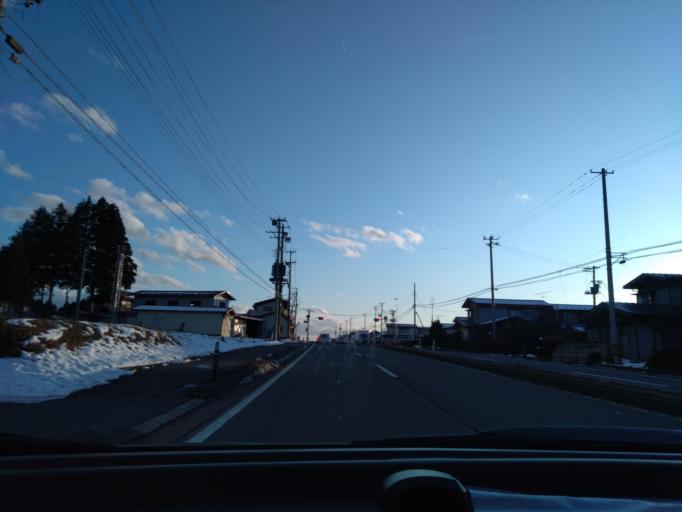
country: JP
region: Iwate
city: Hanamaki
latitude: 39.5280
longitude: 141.1633
